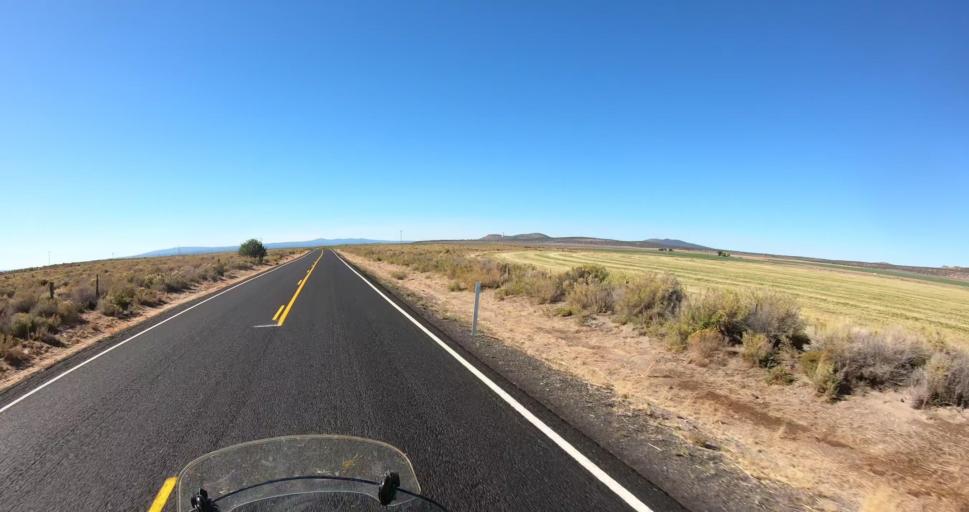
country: US
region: Oregon
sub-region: Deschutes County
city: La Pine
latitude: 43.1289
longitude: -120.8973
